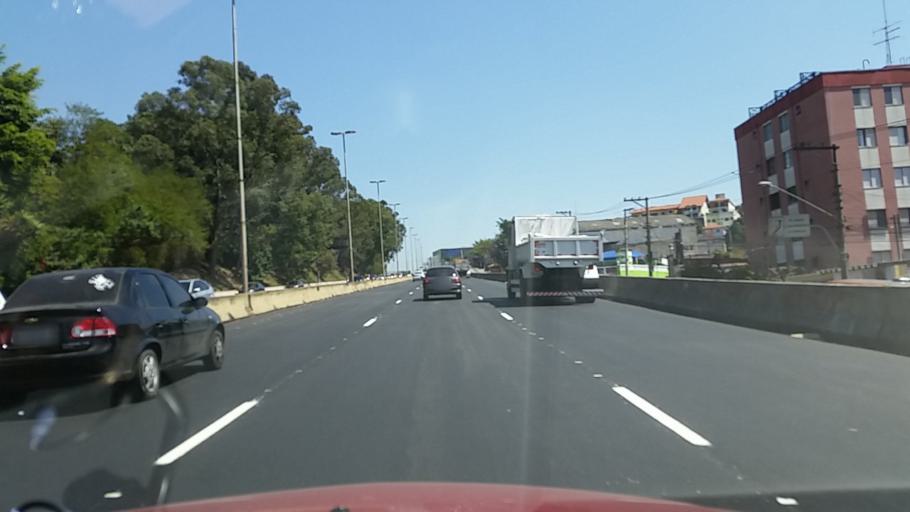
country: BR
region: Sao Paulo
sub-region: Taboao Da Serra
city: Taboao da Serra
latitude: -23.5850
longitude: -46.7417
